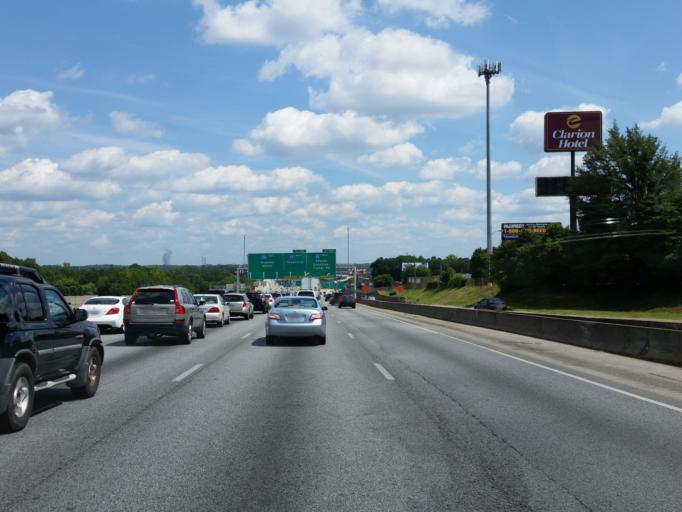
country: US
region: Georgia
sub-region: DeKalb County
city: Doraville
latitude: 33.9011
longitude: -84.2715
